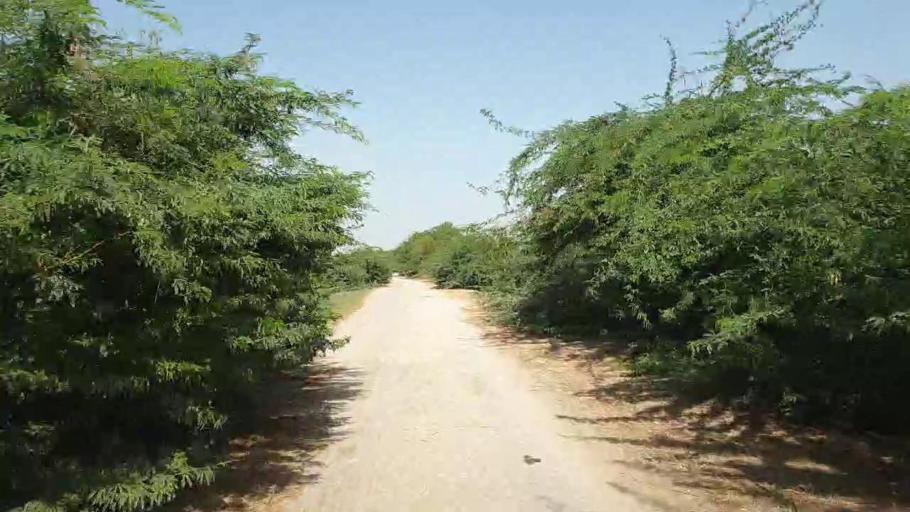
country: PK
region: Sindh
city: Tando Bago
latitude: 24.7630
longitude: 69.0233
